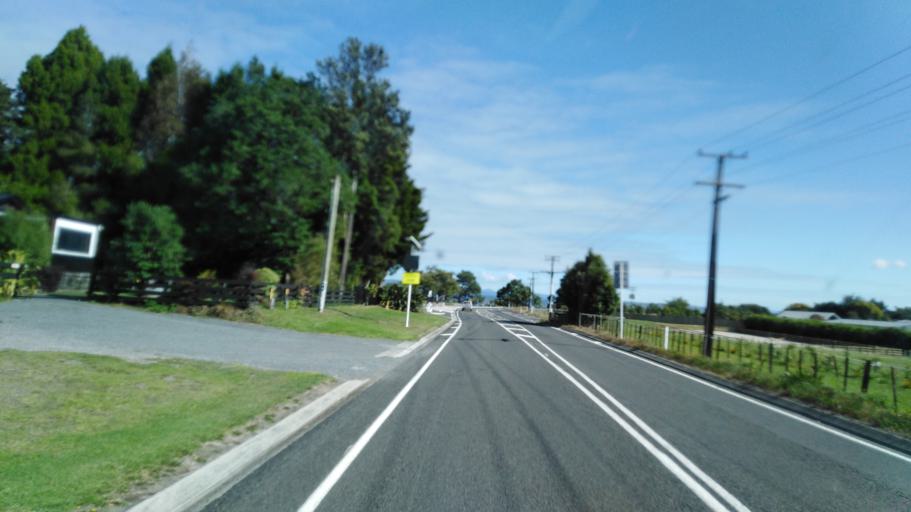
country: NZ
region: Bay of Plenty
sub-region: Tauranga City
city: Tauranga
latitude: -37.8196
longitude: 176.1270
